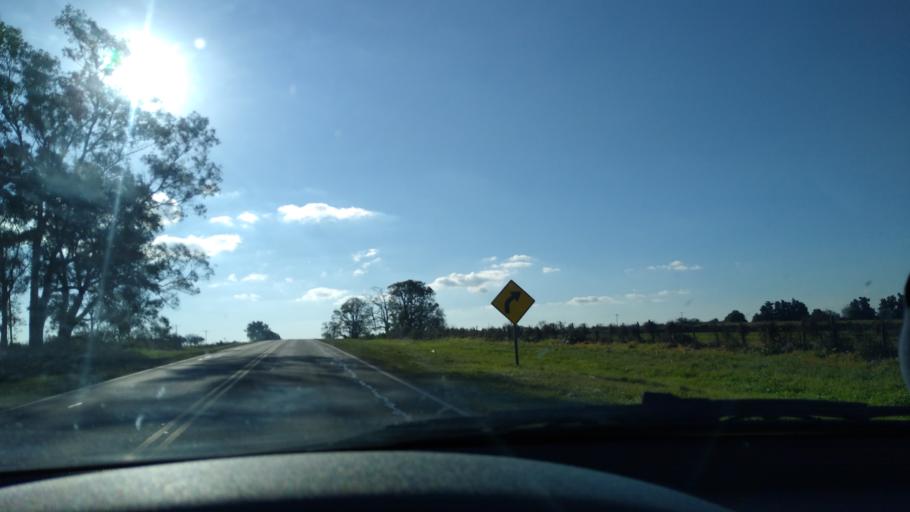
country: AR
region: Entre Rios
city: Diamante
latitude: -32.1245
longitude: -60.5642
